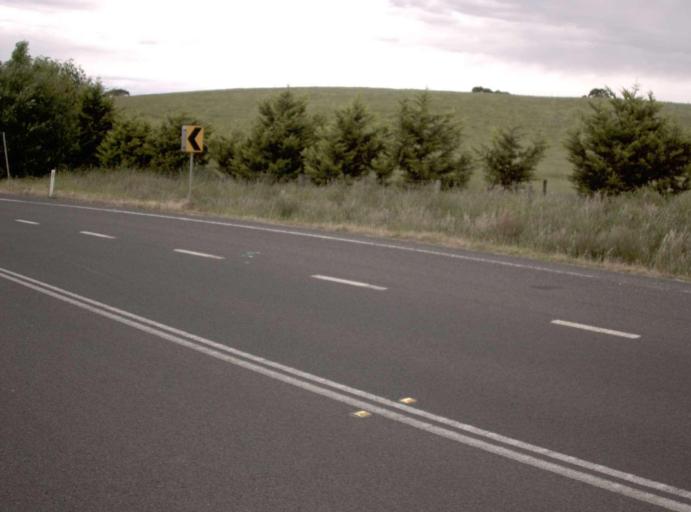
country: AU
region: Victoria
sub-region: Baw Baw
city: Warragul
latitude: -38.4485
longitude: 145.8906
